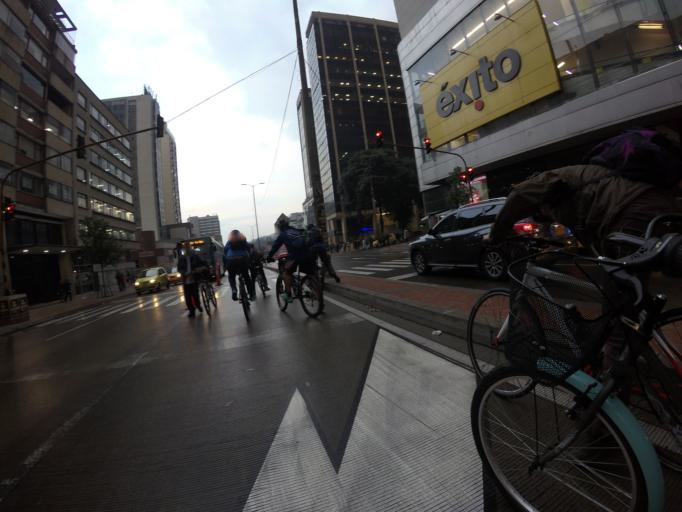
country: CO
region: Bogota D.C.
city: Bogota
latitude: 4.6198
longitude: -74.0681
